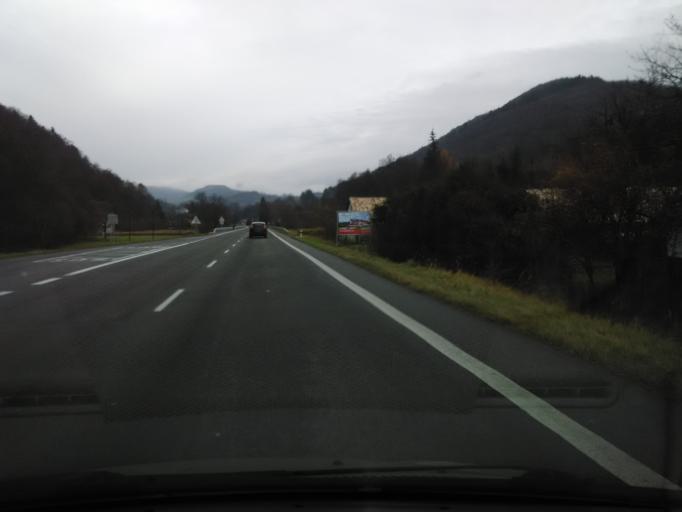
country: SK
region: Banskobystricky
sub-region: Okres Ziar nad Hronom
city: Kremnica
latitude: 48.6643
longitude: 18.9115
